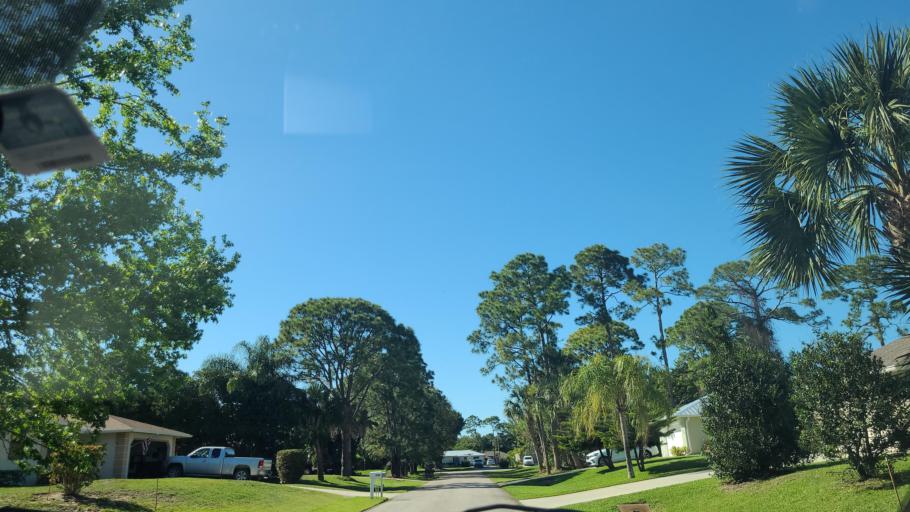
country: US
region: Florida
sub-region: Indian River County
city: Sebastian
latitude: 27.7605
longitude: -80.4766
